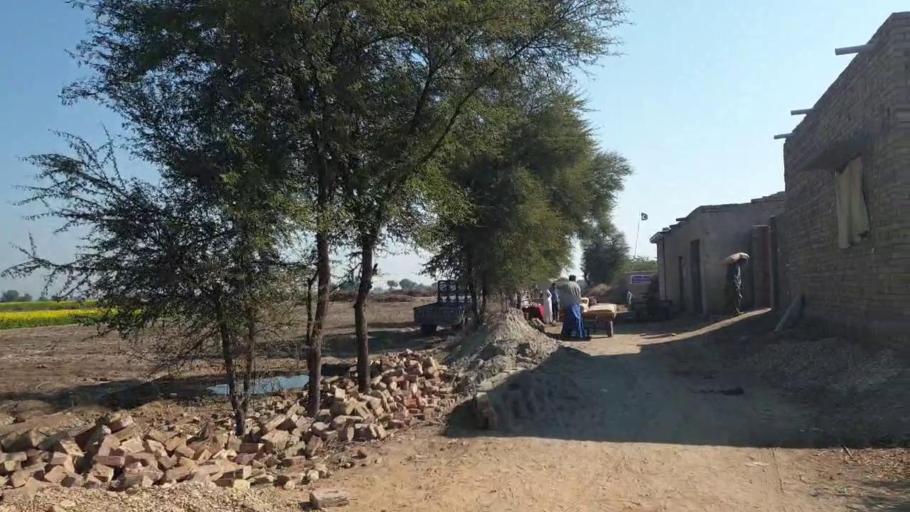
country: PK
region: Sindh
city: Shahpur Chakar
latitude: 26.0810
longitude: 68.6272
